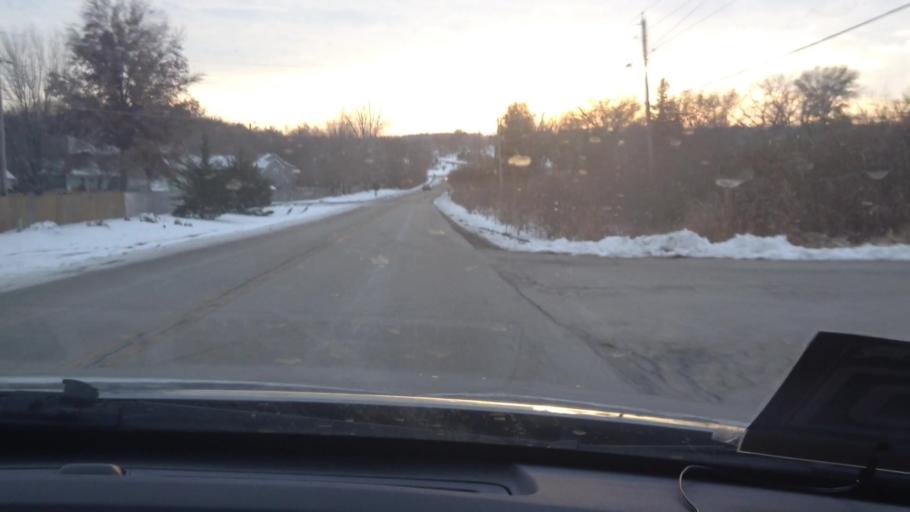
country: US
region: Kansas
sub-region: Leavenworth County
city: Leavenworth
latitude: 39.2849
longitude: -94.9448
